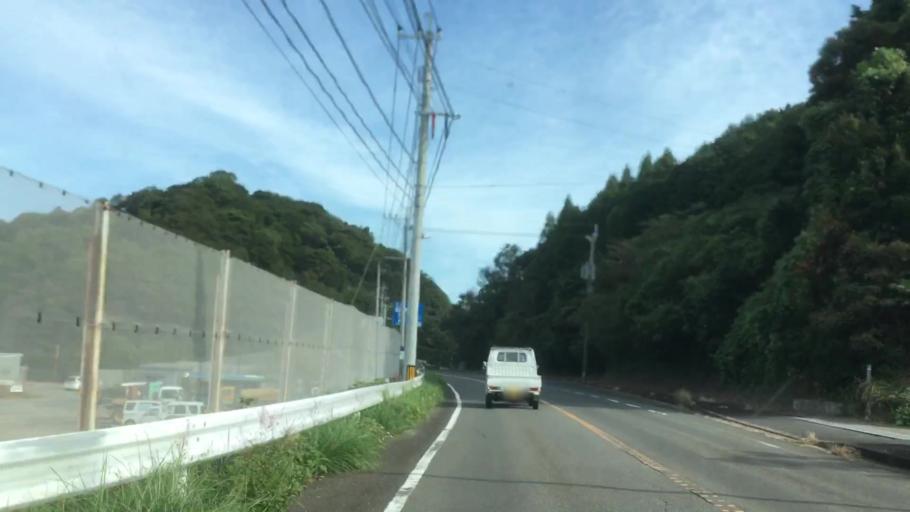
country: JP
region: Nagasaki
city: Sasebo
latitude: 33.0316
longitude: 129.6597
